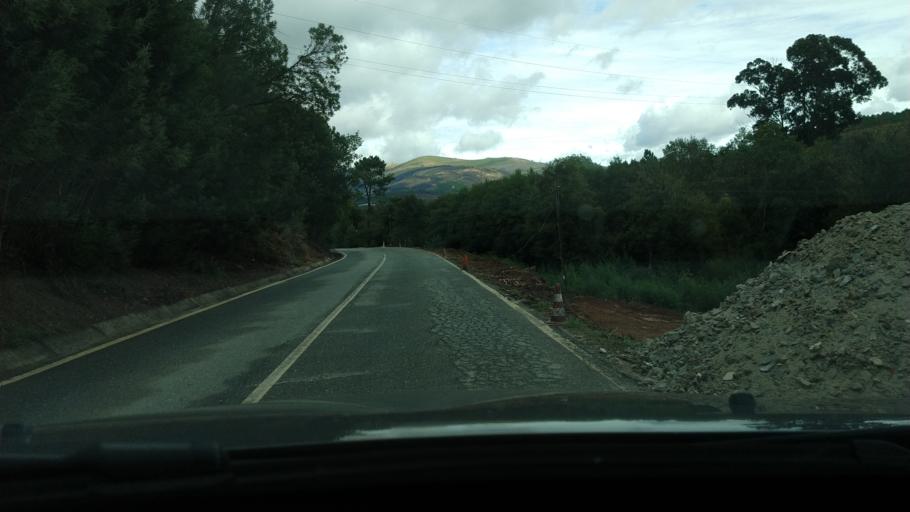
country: PT
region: Castelo Branco
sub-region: Covilha
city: Covilha
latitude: 40.2284
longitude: -7.6076
